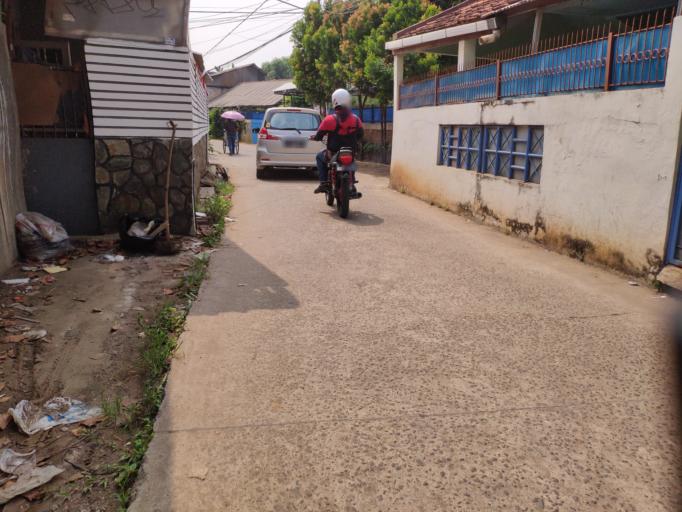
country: ID
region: West Java
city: Pamulang
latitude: -6.3216
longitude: 106.8021
